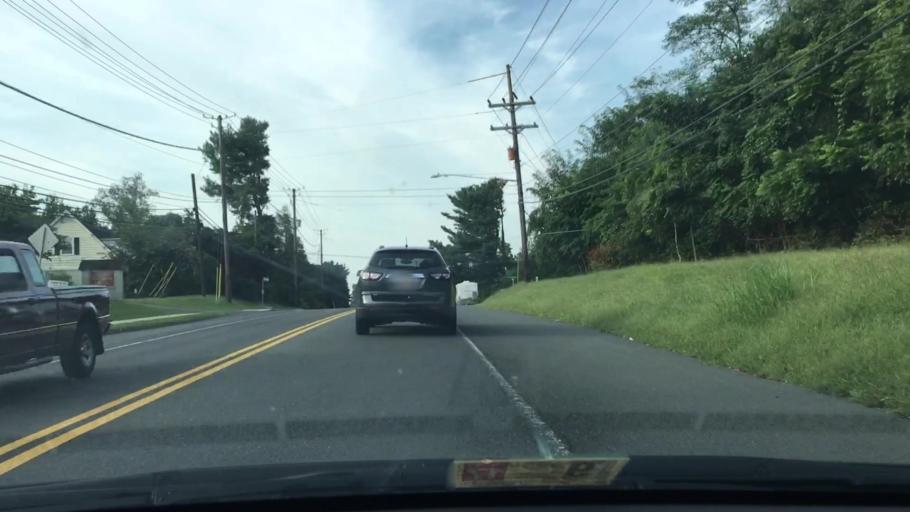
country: US
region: Maryland
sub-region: Montgomery County
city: Rockville
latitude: 39.0546
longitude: -77.1629
